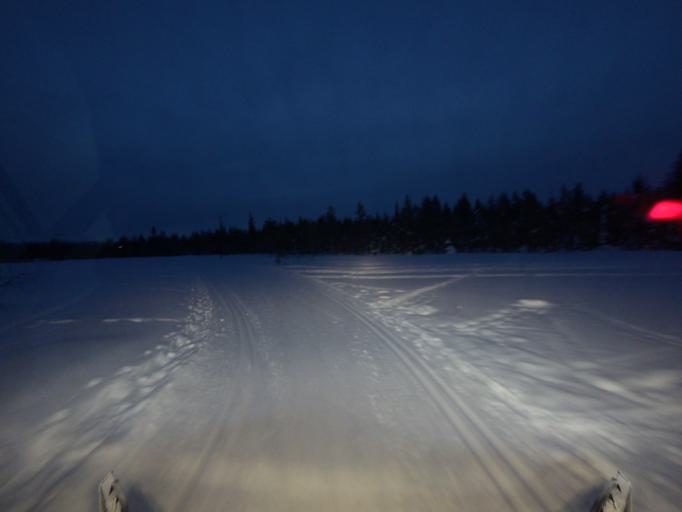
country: FI
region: Lapland
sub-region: Tunturi-Lappi
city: Kolari
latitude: 67.6040
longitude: 24.1347
